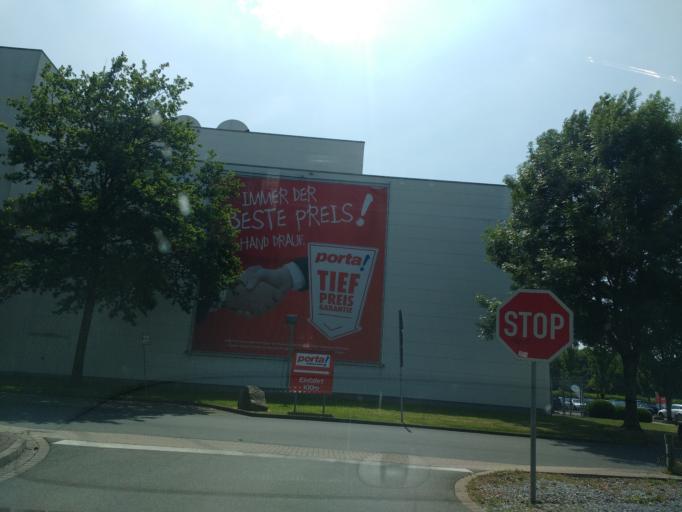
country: DE
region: North Rhine-Westphalia
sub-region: Regierungsbezirk Detmold
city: Oerlinghausen
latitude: 51.9989
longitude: 8.6099
